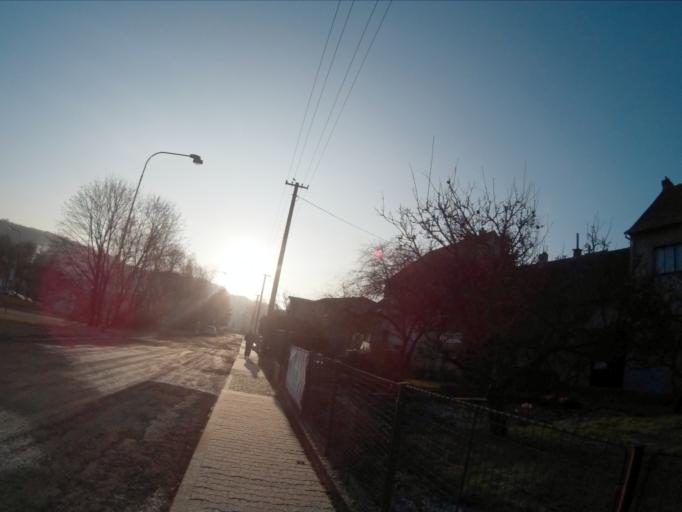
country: CZ
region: Vysocina
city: Namest' nad Oslavou
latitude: 49.2058
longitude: 16.1537
